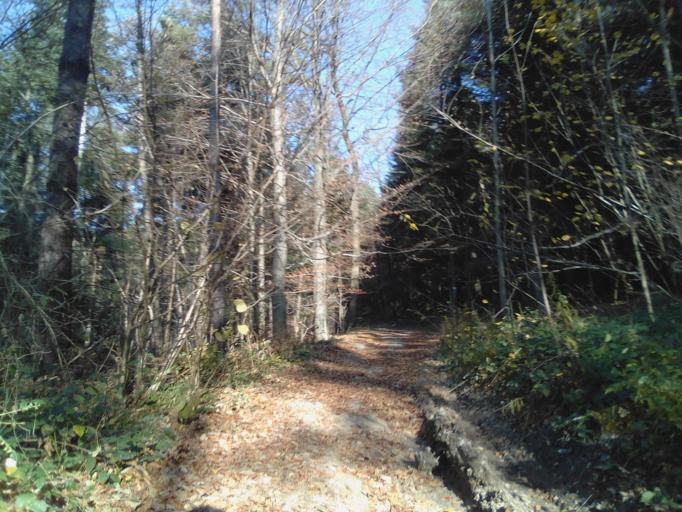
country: PL
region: Subcarpathian Voivodeship
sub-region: Powiat strzyzowski
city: Wysoka Strzyzowska
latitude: 49.8009
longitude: 21.7265
